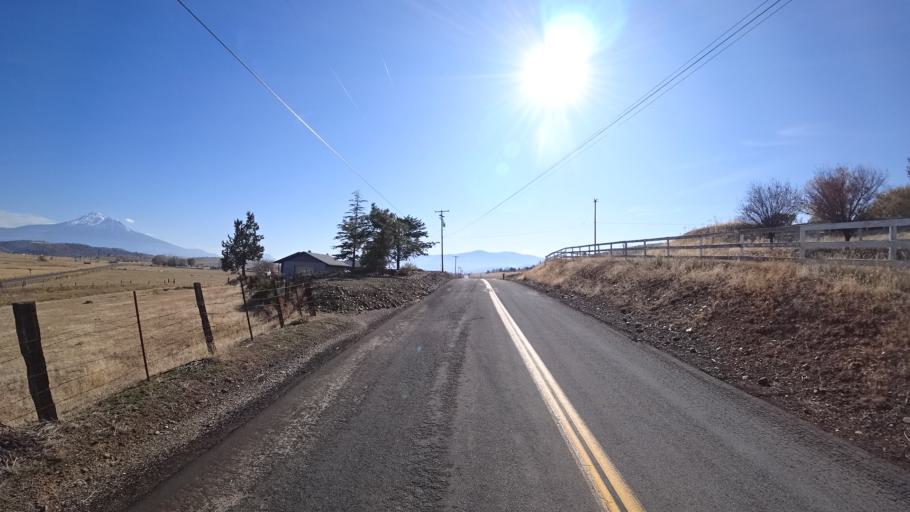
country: US
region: California
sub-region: Siskiyou County
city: Montague
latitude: 41.6081
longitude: -122.5297
